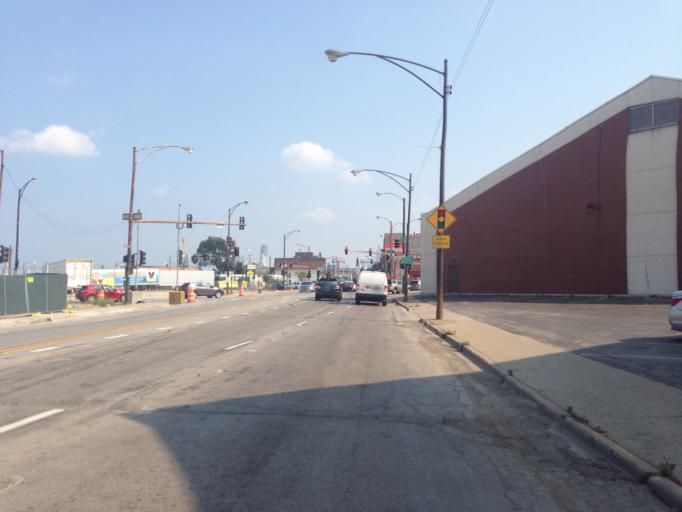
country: US
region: Illinois
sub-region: Cook County
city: Chicago
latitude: 41.9258
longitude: -87.6786
